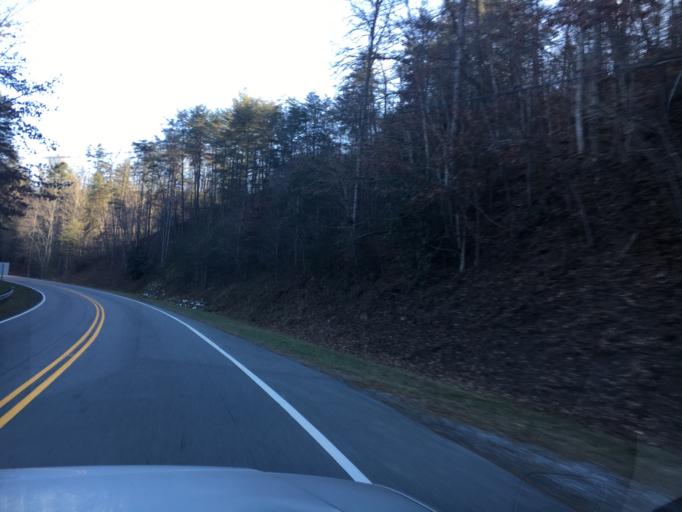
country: US
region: North Carolina
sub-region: McDowell County
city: West Marion
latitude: 35.5553
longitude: -81.9701
